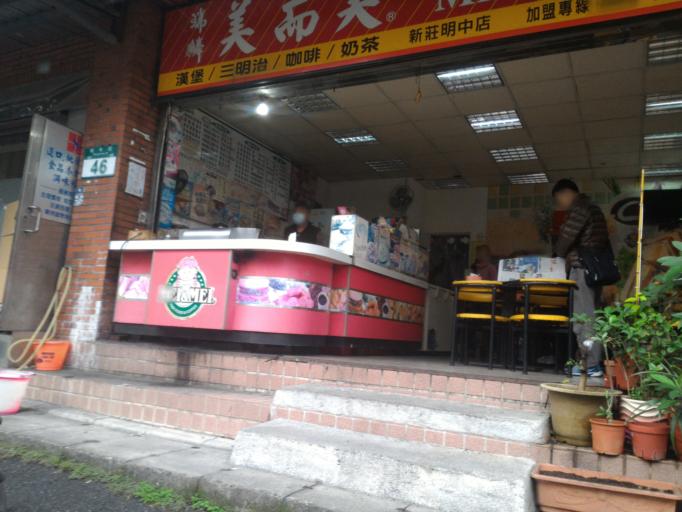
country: TW
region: Taipei
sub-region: Taipei
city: Banqiao
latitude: 25.0399
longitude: 121.4568
